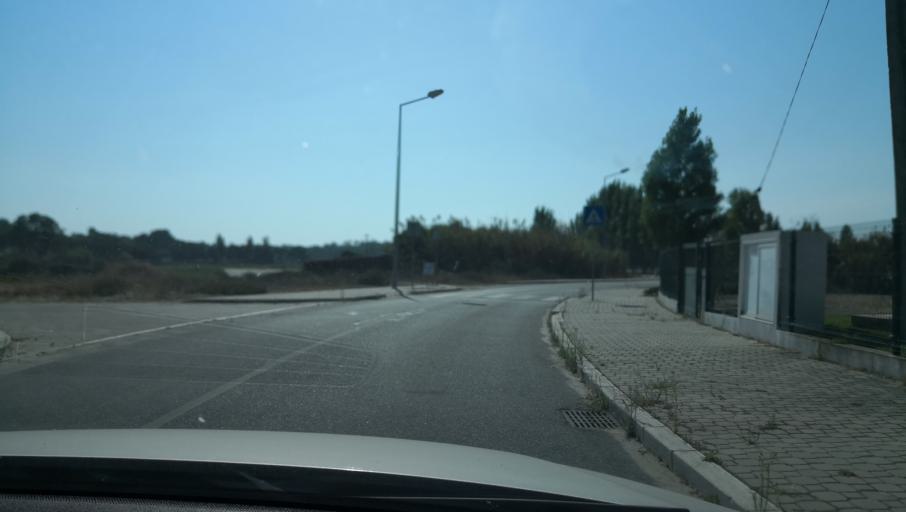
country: PT
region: Setubal
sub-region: Setubal
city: Setubal
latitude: 38.3967
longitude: -8.7731
